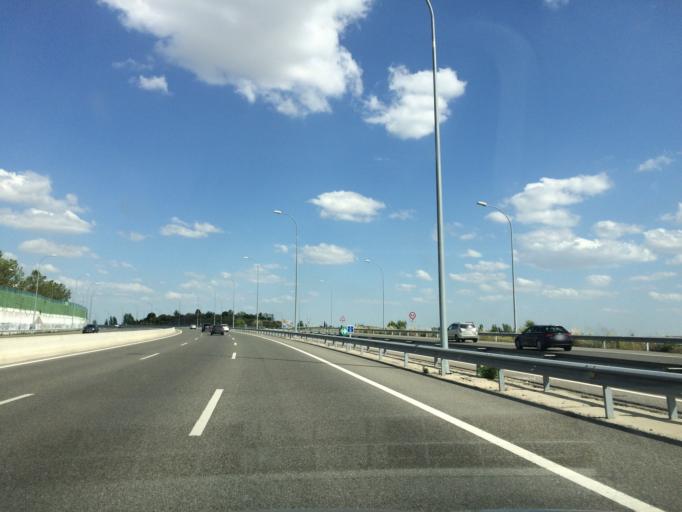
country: ES
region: Madrid
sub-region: Provincia de Madrid
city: Hortaleza
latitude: 40.4737
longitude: -3.6281
